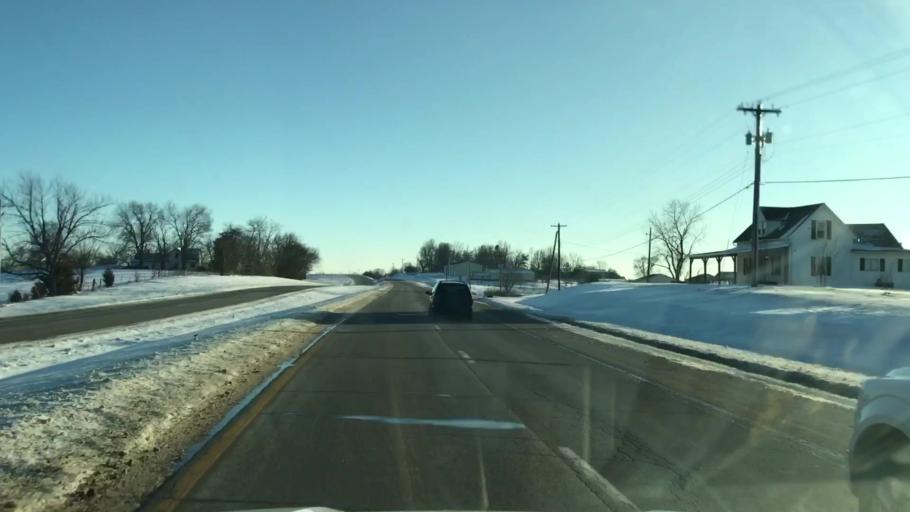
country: US
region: Missouri
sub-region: Andrew County
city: Country Club Village
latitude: 39.8825
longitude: -94.8085
